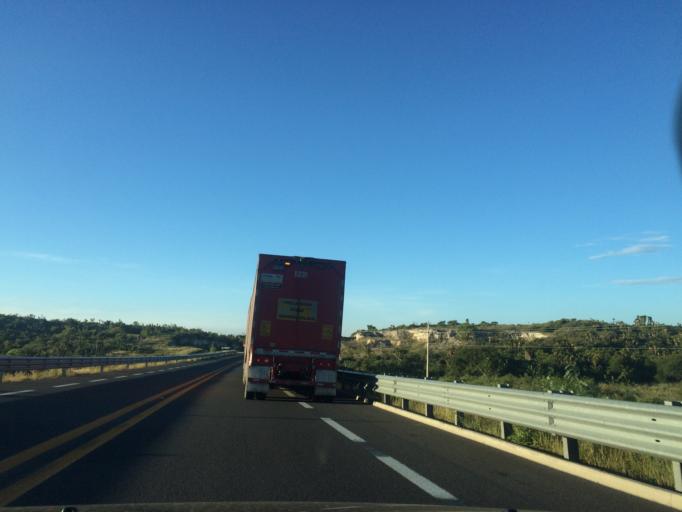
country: MX
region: Puebla
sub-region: Tehuacan
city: Magdalena Cuayucatepec
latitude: 18.5796
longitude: -97.4653
